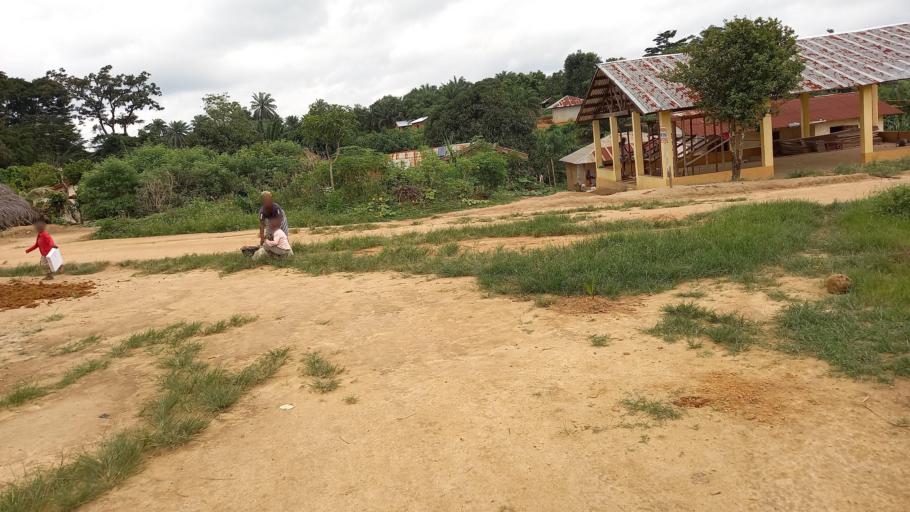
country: SL
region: Eastern Province
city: Kailahun
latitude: 8.2860
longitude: -10.5710
